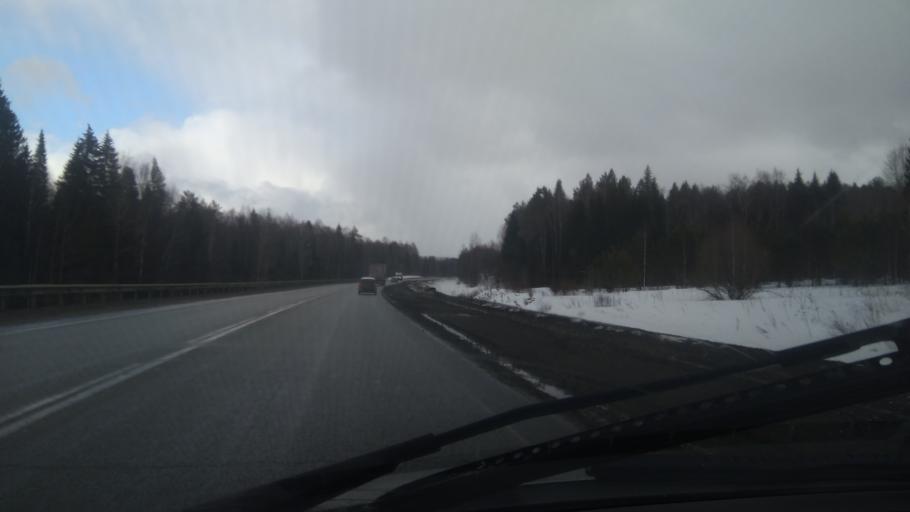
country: RU
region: Sverdlovsk
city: Ufimskiy
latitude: 56.7871
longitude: 58.3810
